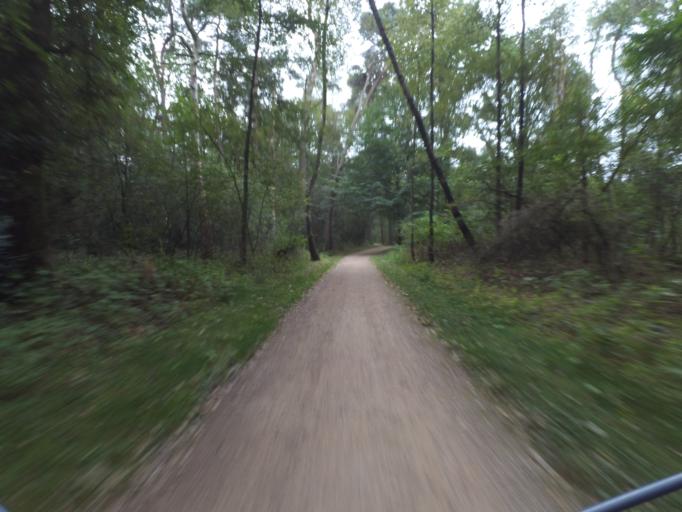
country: DE
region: Lower Saxony
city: Nordhorn
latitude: 52.3411
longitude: 7.0542
